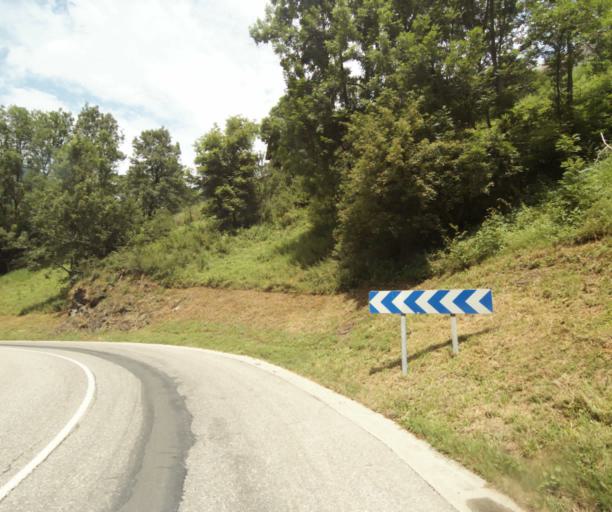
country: FR
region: Rhone-Alpes
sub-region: Departement de la Haute-Savoie
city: Thones
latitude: 45.8599
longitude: 6.3286
